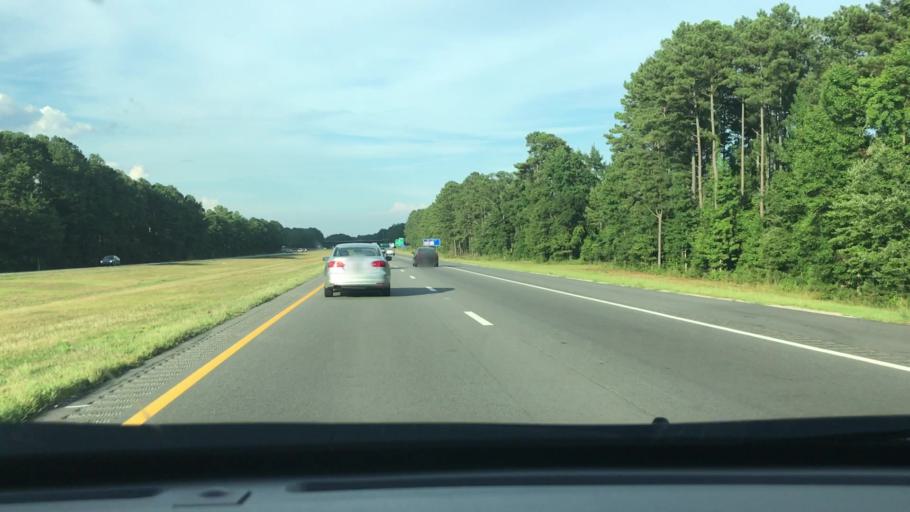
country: US
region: North Carolina
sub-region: Cumberland County
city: Hope Mills
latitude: 34.9347
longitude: -78.9324
